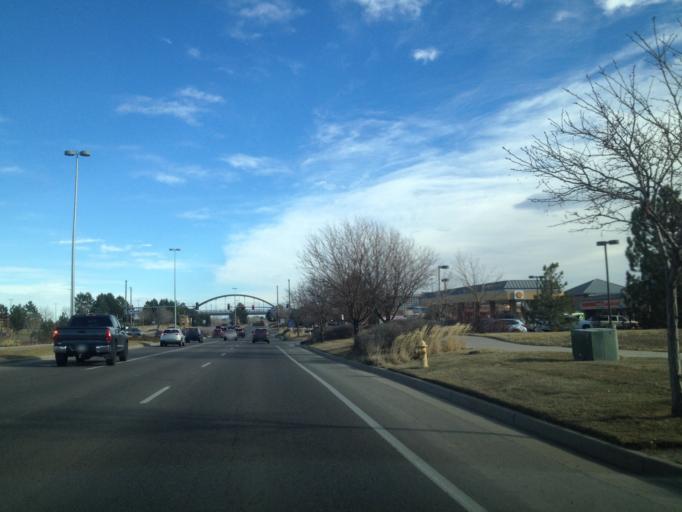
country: US
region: Colorado
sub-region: Boulder County
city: Superior
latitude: 39.9287
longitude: -105.1390
